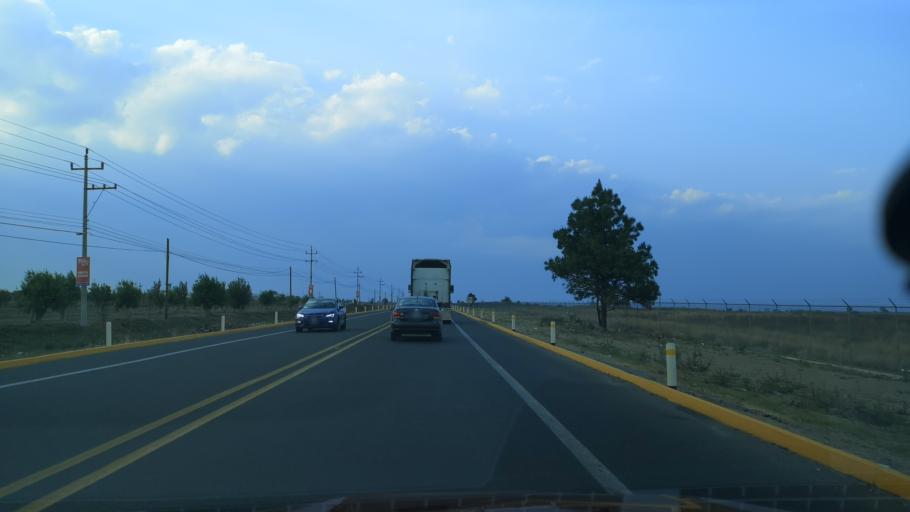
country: MX
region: Puebla
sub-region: Juan C. Bonilla
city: Santa Maria Zacatepec
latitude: 19.1463
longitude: -98.3741
